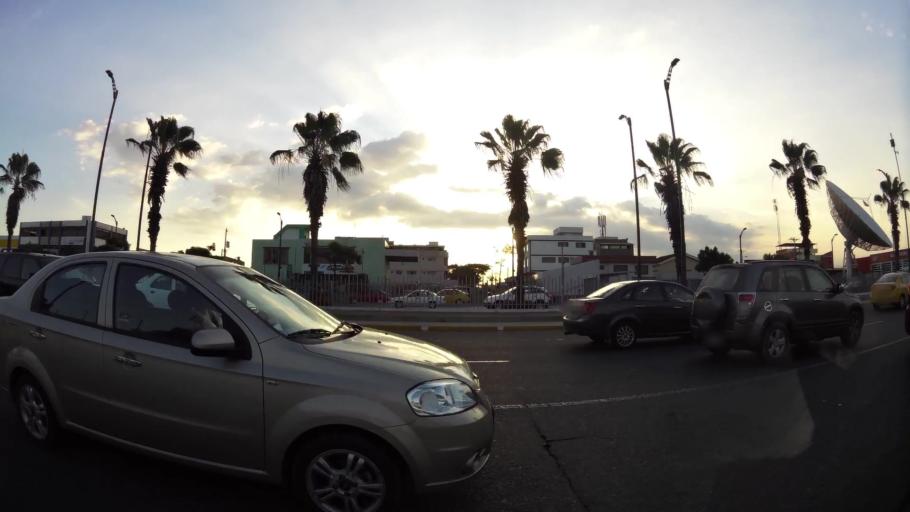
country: EC
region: Guayas
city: Eloy Alfaro
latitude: -2.1480
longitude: -79.8861
